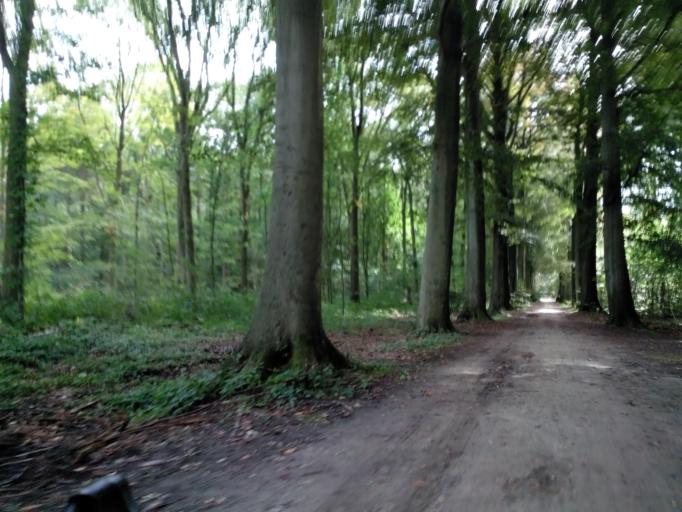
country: BE
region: Flanders
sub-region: Provincie Vlaams-Brabant
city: Oud-Heverlee
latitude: 50.8519
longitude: 4.6822
